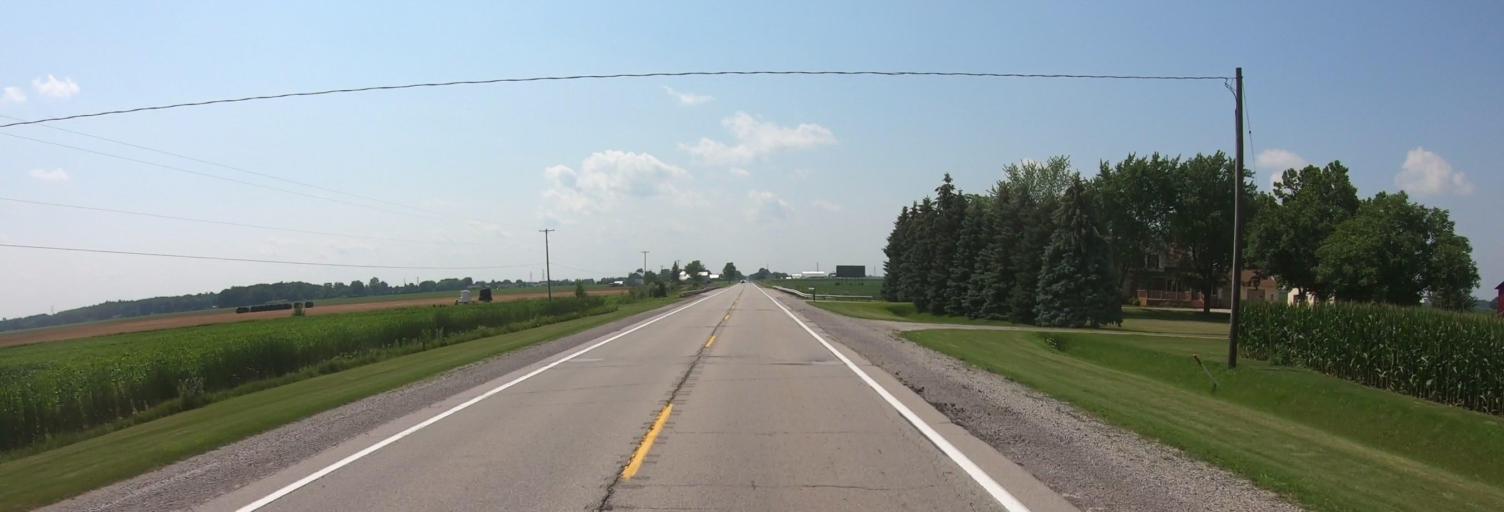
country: US
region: Michigan
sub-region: Saginaw County
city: Frankenmuth
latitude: 43.4073
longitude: -83.7637
